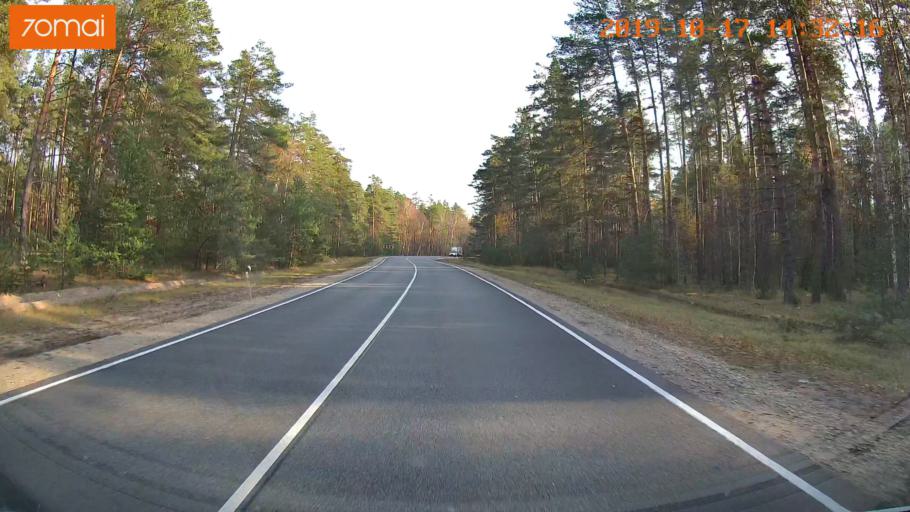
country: RU
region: Rjazan
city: Solotcha
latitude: 54.9290
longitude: 39.9765
